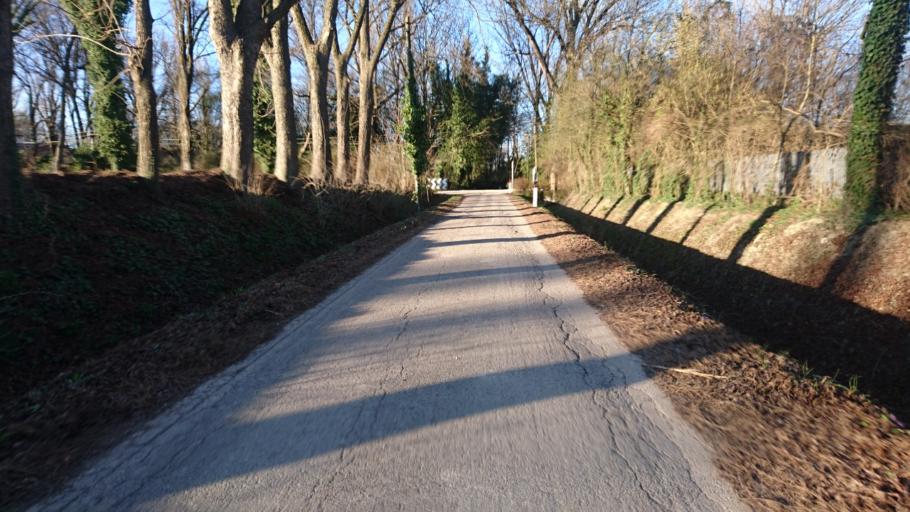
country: IT
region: Veneto
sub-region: Provincia di Padova
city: Bertipaglia
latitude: 45.3020
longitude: 11.8863
